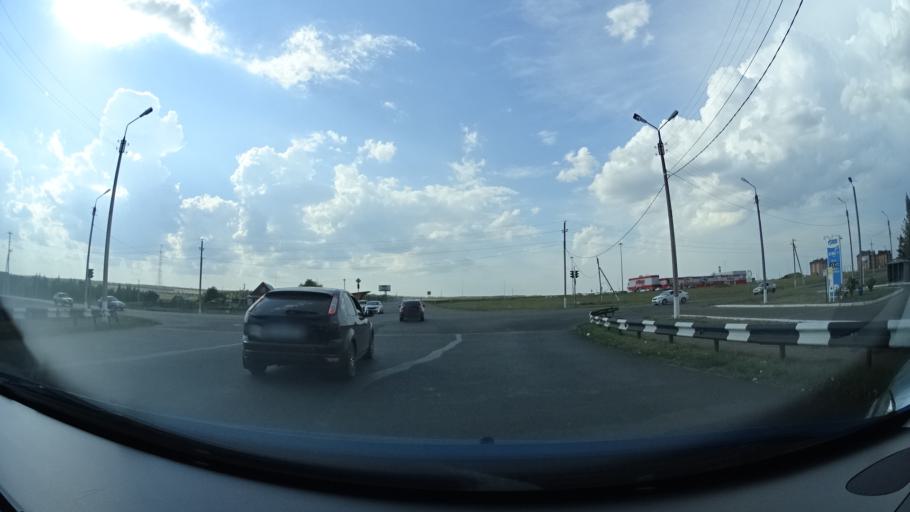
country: RU
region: Bashkortostan
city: Meleuz
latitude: 52.9641
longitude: 55.9107
